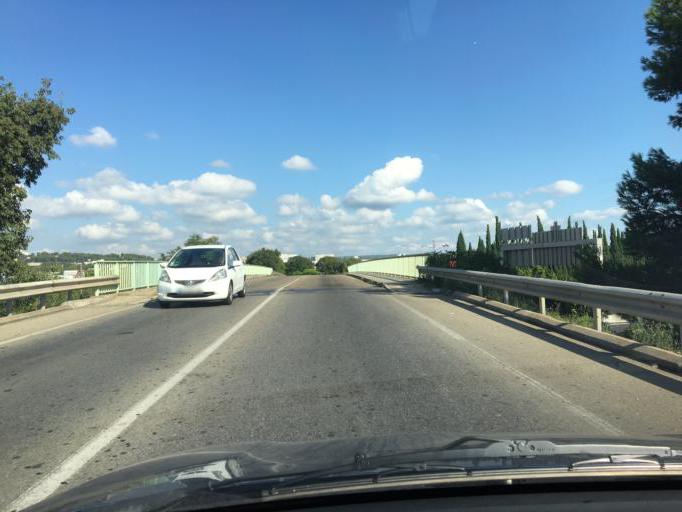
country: FR
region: Languedoc-Roussillon
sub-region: Departement du Gard
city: Nimes
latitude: 43.8119
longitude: 4.3545
